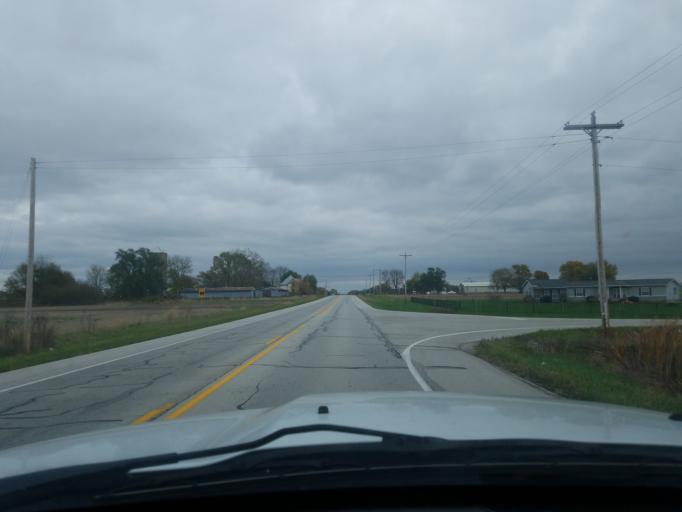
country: US
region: Indiana
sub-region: Shelby County
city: Shelbyville
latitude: 39.4958
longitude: -85.8997
